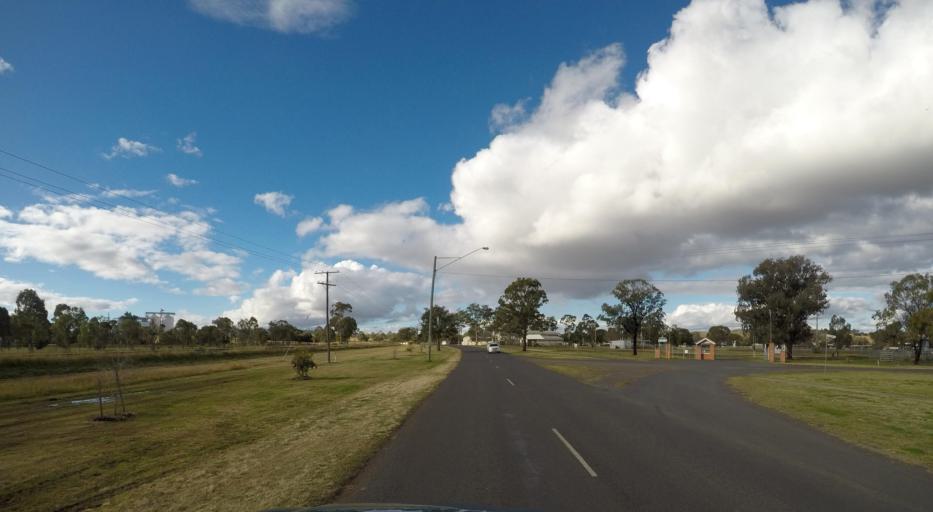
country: AU
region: Queensland
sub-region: Toowoomba
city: Westbrook
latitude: -27.7126
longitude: 151.6394
